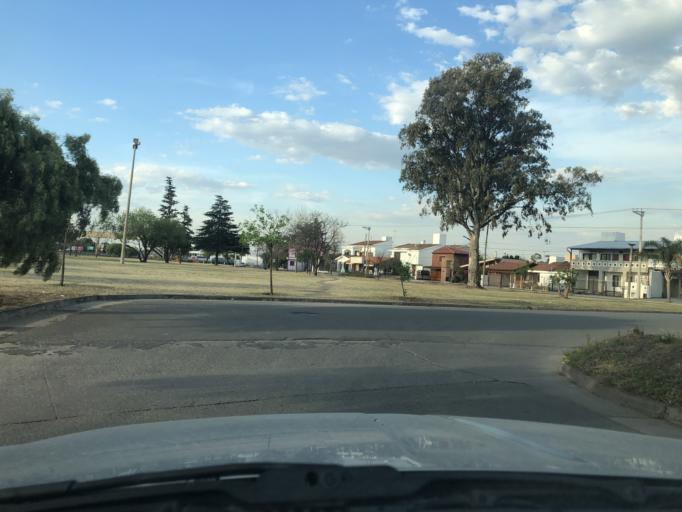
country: AR
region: Cordoba
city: Jesus Maria
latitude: -30.9808
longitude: -64.0857
